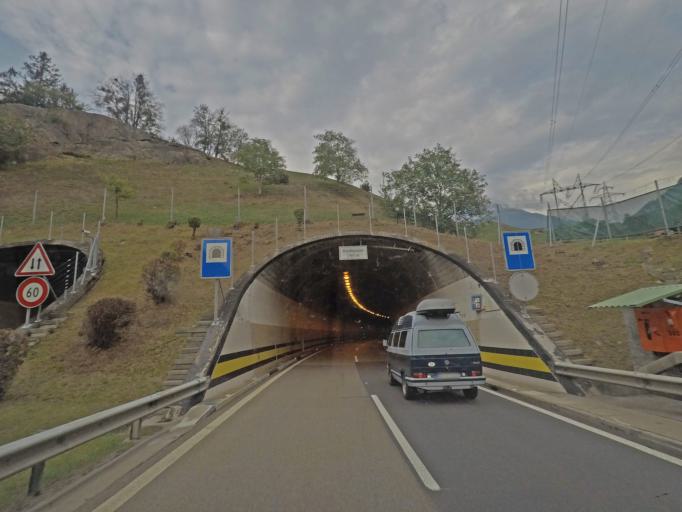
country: CH
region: Uri
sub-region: Uri
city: Silenen
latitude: 46.7569
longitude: 8.6492
